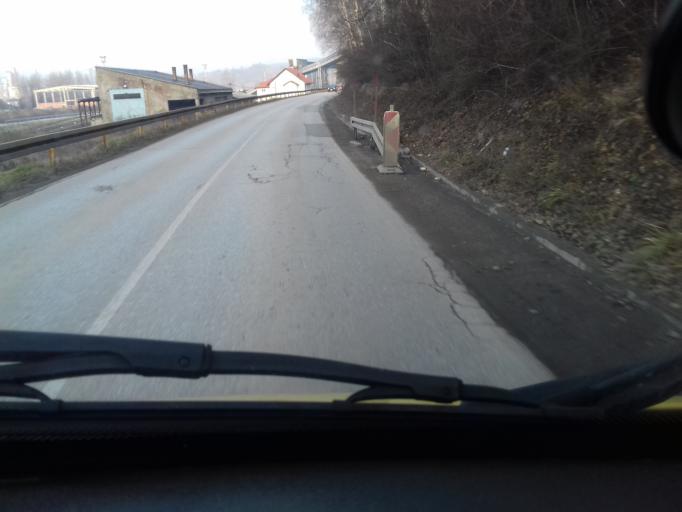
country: BA
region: Federation of Bosnia and Herzegovina
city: Kakanj
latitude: 44.1023
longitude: 18.1123
